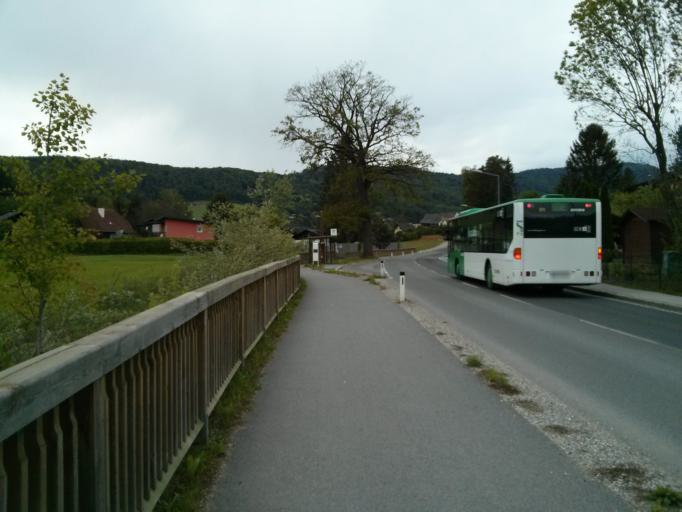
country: AT
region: Styria
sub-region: Politischer Bezirk Graz-Umgebung
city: Stattegg
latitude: 47.1339
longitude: 15.4223
